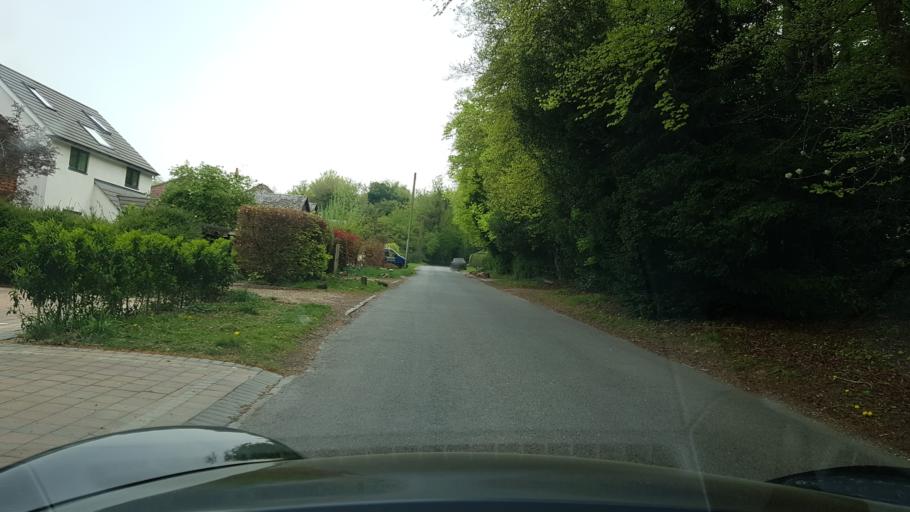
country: GB
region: England
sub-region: Surrey
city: East Horsley
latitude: 51.2566
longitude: -0.4514
